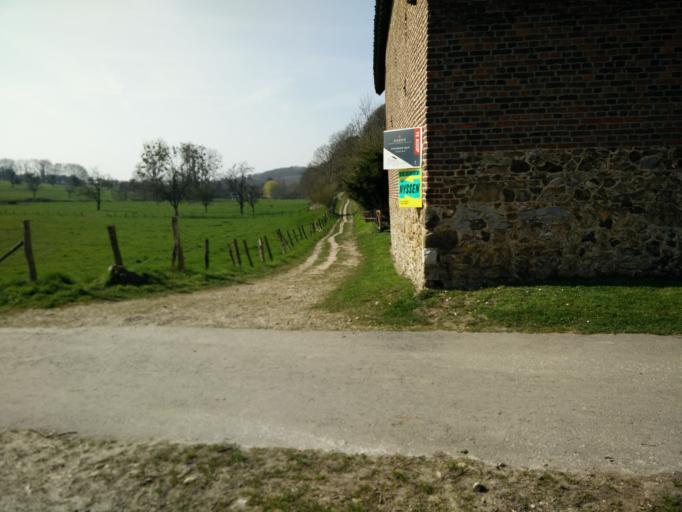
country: BE
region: Flanders
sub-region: Provincie Limburg
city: Sint-Pieters-Voeren
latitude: 50.7550
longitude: 5.7875
